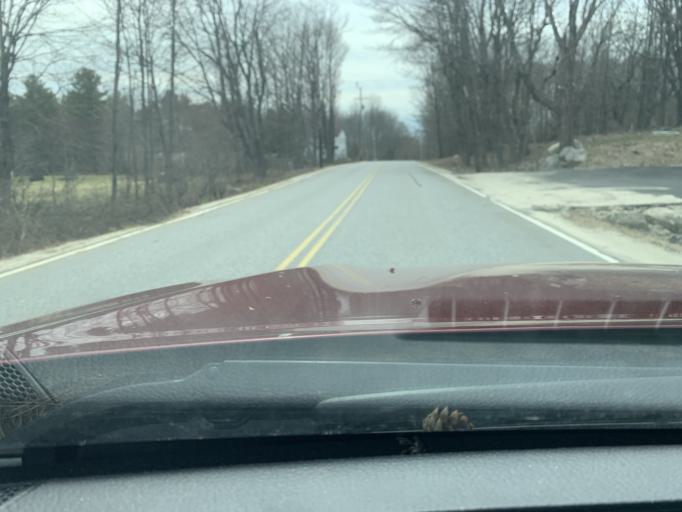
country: US
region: Maine
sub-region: Cumberland County
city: Raymond
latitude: 43.9567
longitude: -70.3881
